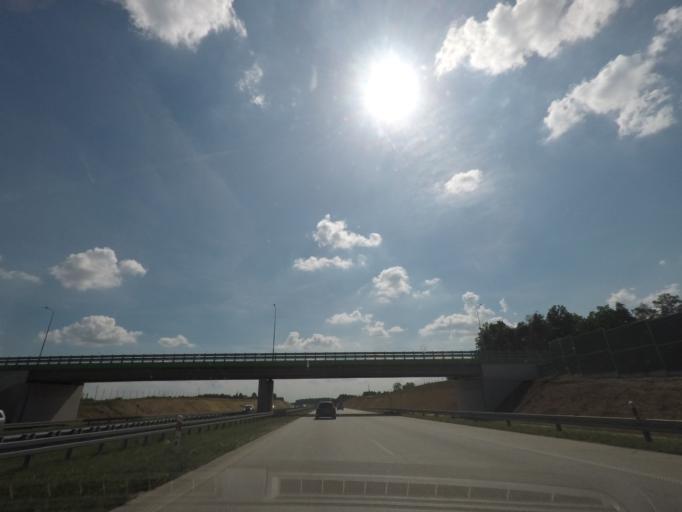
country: PL
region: Lodz Voivodeship
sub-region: Powiat lodzki wschodni
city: Andrespol
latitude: 51.7795
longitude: 19.6080
